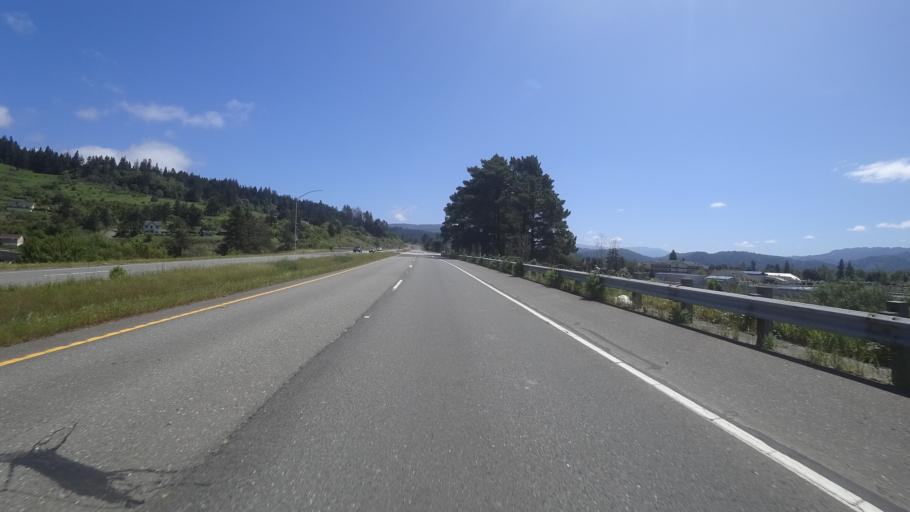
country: US
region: California
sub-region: Humboldt County
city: Blue Lake
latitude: 40.8886
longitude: -124.0024
